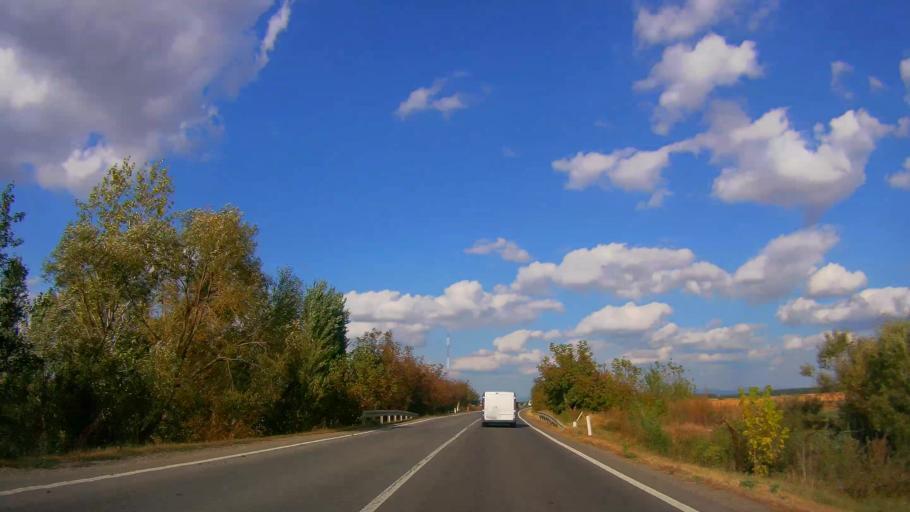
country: RO
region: Satu Mare
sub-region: Comuna Botiz
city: Botiz
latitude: 47.8467
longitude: 22.9674
